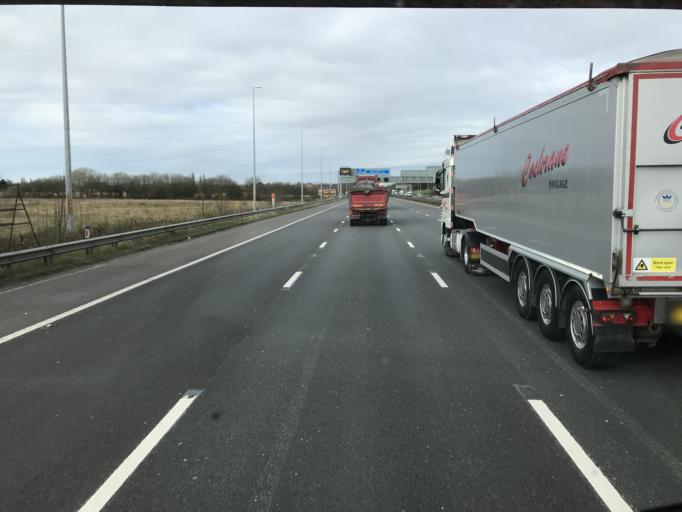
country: GB
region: England
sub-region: Warrington
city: Winwick
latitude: 53.4217
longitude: -2.5857
